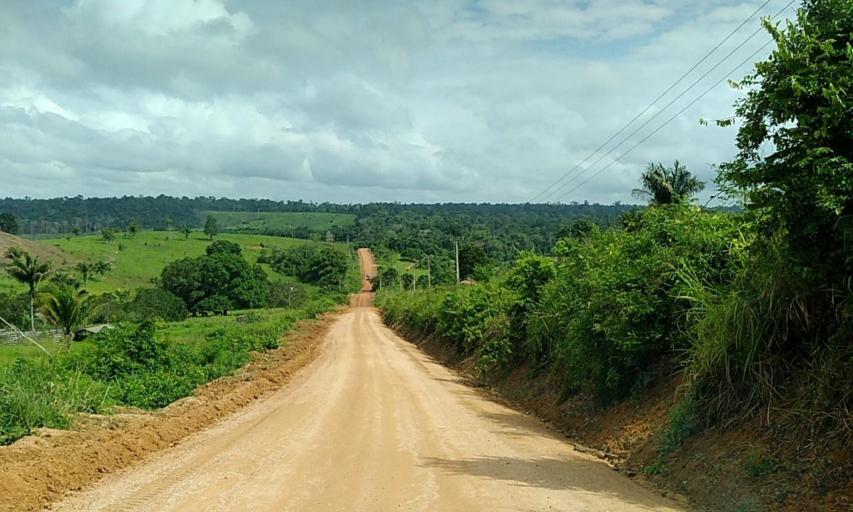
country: BR
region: Para
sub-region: Senador Jose Porfirio
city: Senador Jose Porfirio
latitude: -3.0650
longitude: -51.6351
